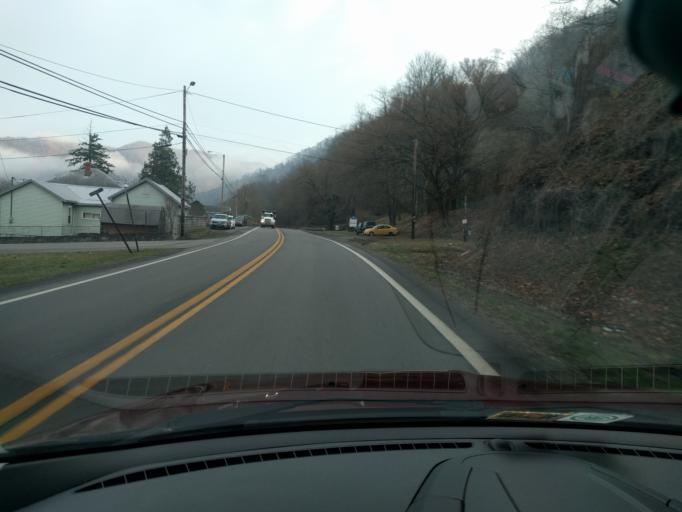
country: US
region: West Virginia
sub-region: Kanawha County
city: Montgomery
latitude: 38.1672
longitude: -81.3030
